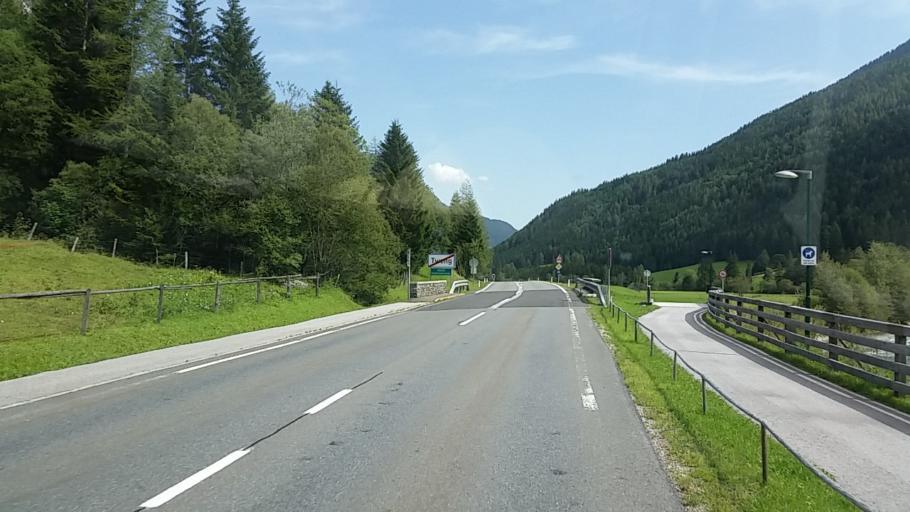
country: AT
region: Salzburg
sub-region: Politischer Bezirk Tamsweg
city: Tweng
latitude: 47.1890
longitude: 13.6036
